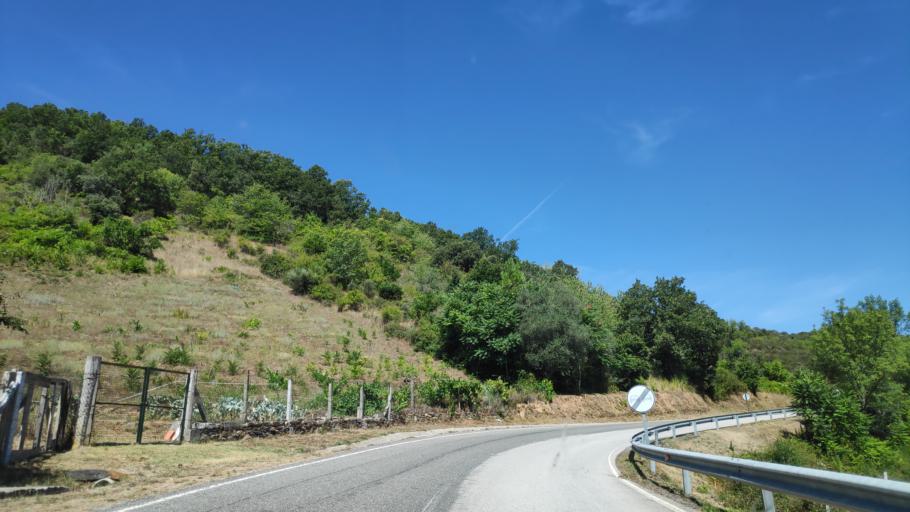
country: PT
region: Braganca
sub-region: Braganca Municipality
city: Braganca
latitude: 41.8965
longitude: -6.7287
